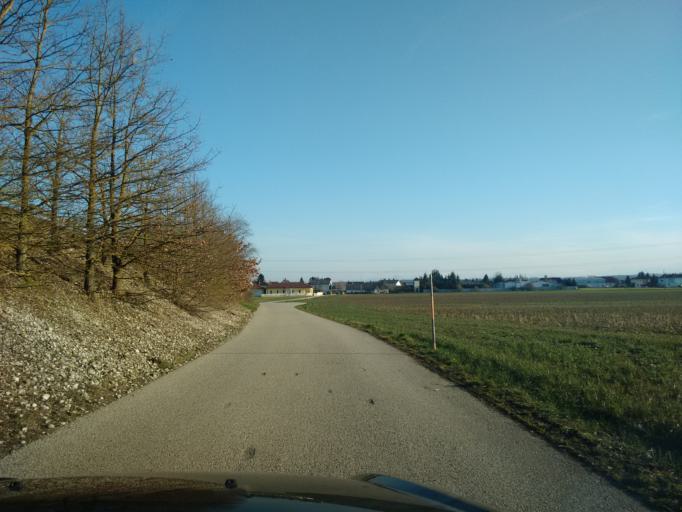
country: AT
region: Upper Austria
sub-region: Wels-Land
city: Marchtrenk
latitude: 48.2061
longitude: 14.1408
